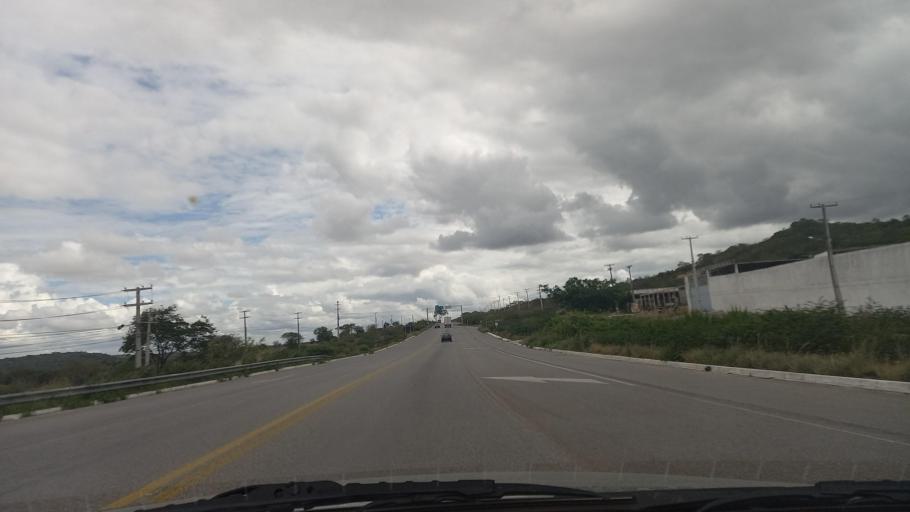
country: BR
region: Pernambuco
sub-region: Cachoeirinha
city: Cachoeirinha
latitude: -8.3309
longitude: -36.1480
